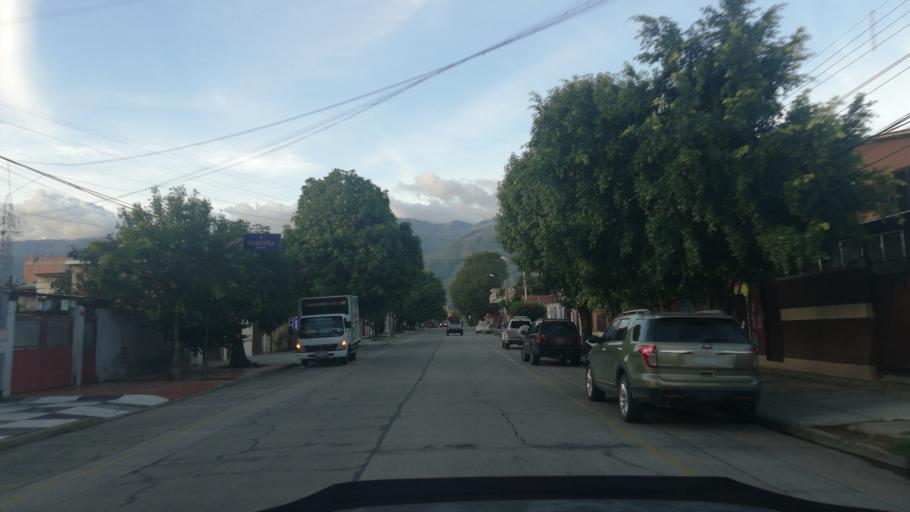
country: BO
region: Cochabamba
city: Cochabamba
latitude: -17.3770
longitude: -66.1879
